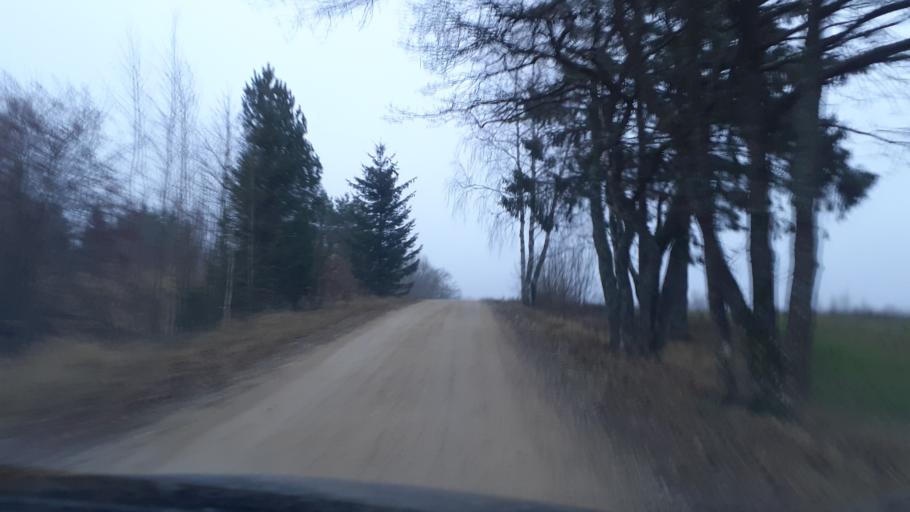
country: LV
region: Alsunga
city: Alsunga
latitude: 56.8766
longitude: 21.7198
